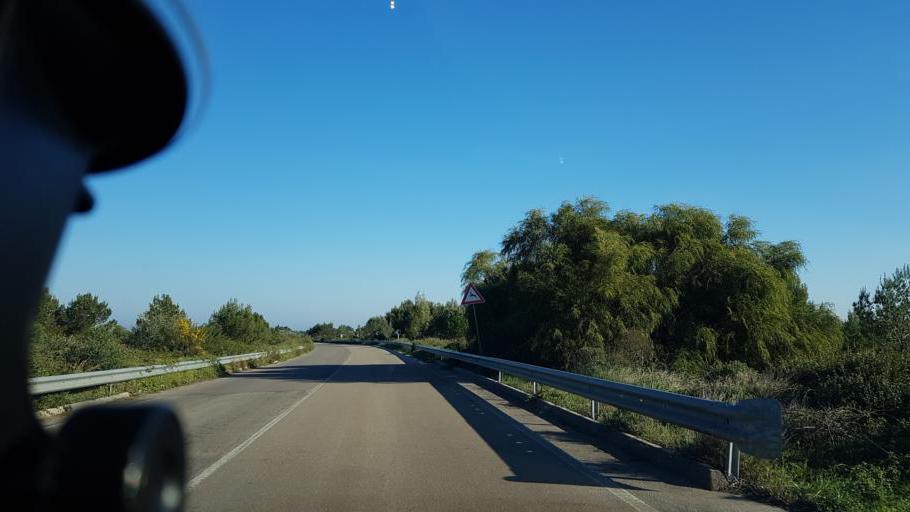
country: IT
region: Apulia
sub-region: Provincia di Lecce
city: Merine
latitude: 40.3959
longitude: 18.2537
